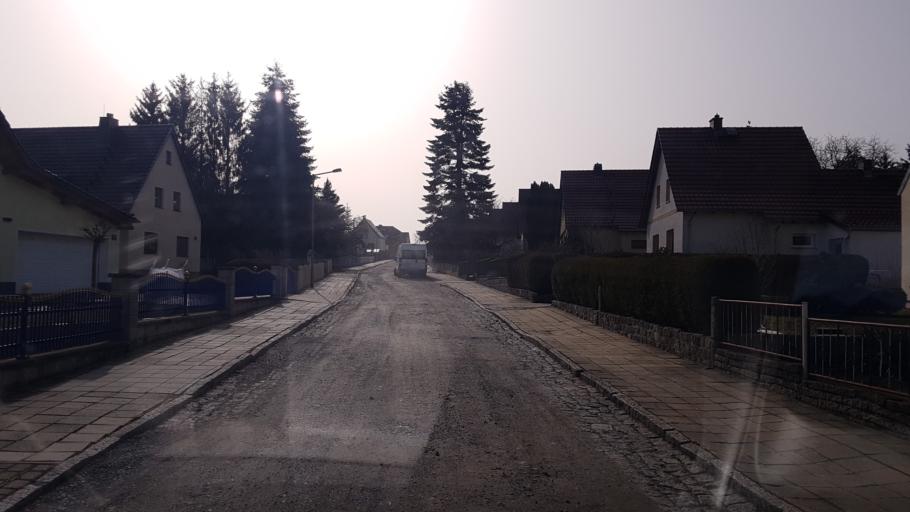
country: DE
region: Brandenburg
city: Lauchhammer
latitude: 51.5072
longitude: 13.7919
